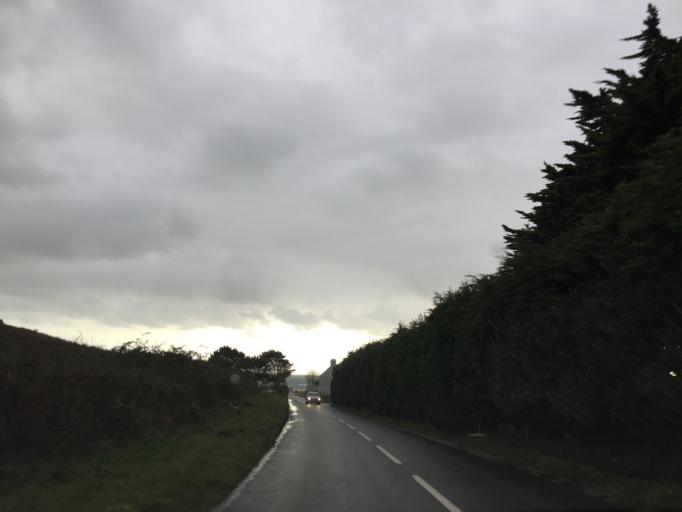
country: JE
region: St Helier
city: Saint Helier
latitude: 49.2339
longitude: -2.2316
